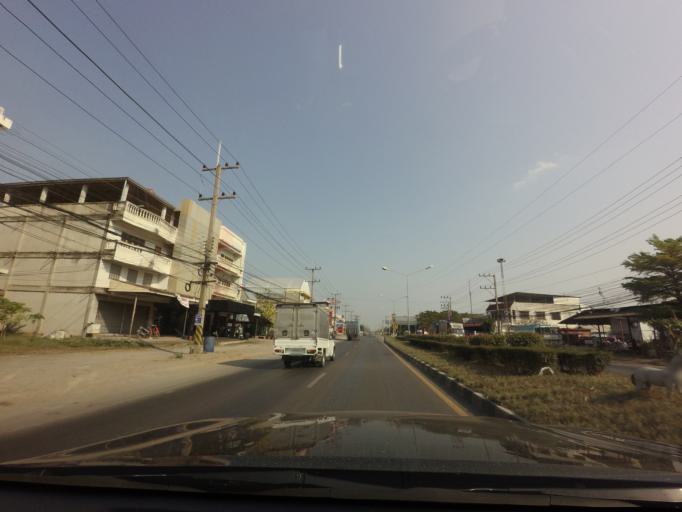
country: TH
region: Kanchanaburi
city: Tha Maka
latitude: 13.8652
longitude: 99.8261
